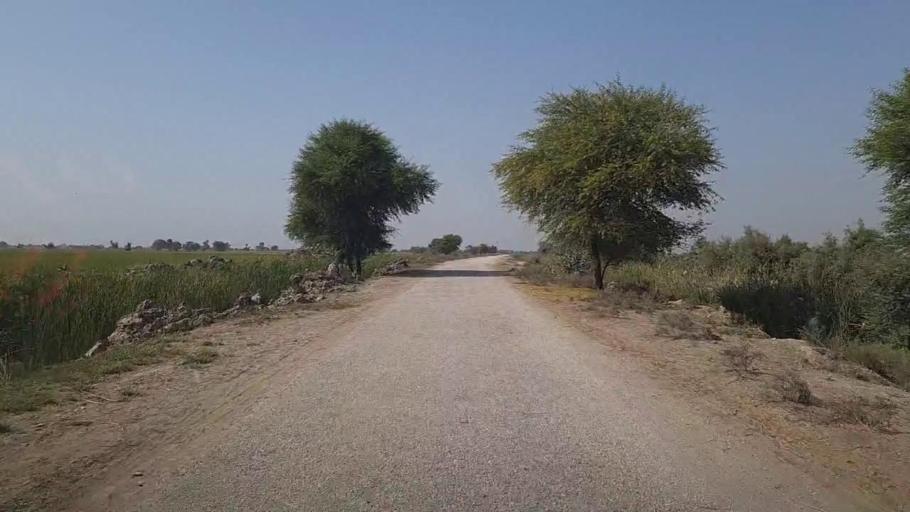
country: PK
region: Sindh
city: Kandhkot
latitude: 28.3950
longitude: 69.2744
